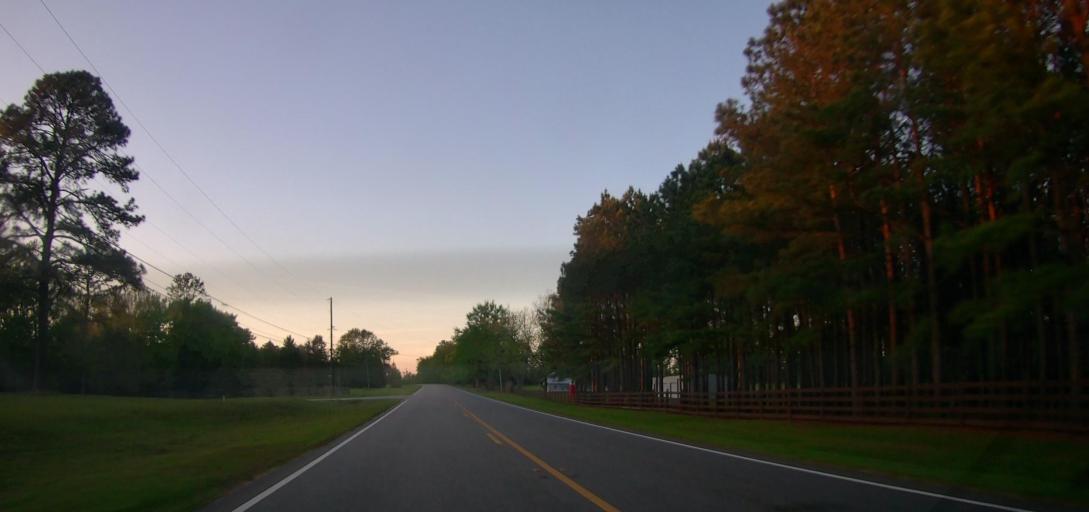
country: US
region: Georgia
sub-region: Marion County
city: Buena Vista
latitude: 32.3445
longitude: -84.5324
